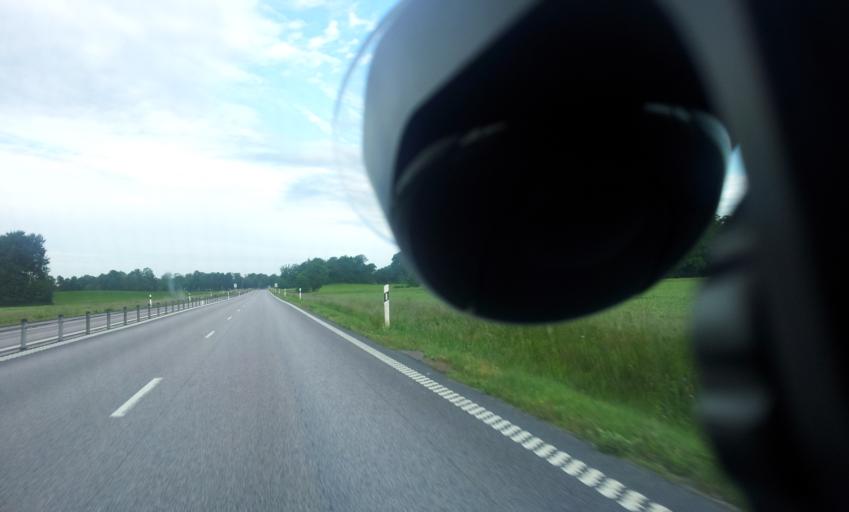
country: SE
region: Kalmar
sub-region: Monsteras Kommun
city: Moensteras
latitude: 57.0651
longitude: 16.4606
